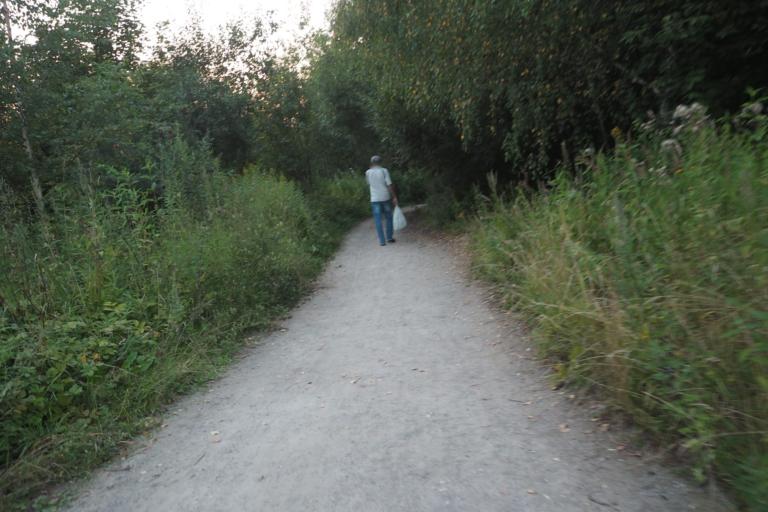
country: RU
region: Moscow
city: Orekhovo-Borisovo Severnoye
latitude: 55.6053
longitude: 37.6953
